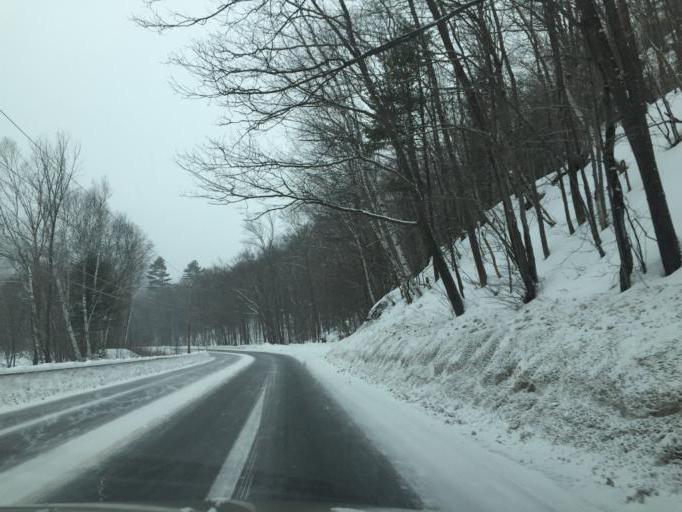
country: US
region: New Hampshire
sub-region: Carroll County
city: North Conway
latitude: 44.1781
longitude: -71.2248
